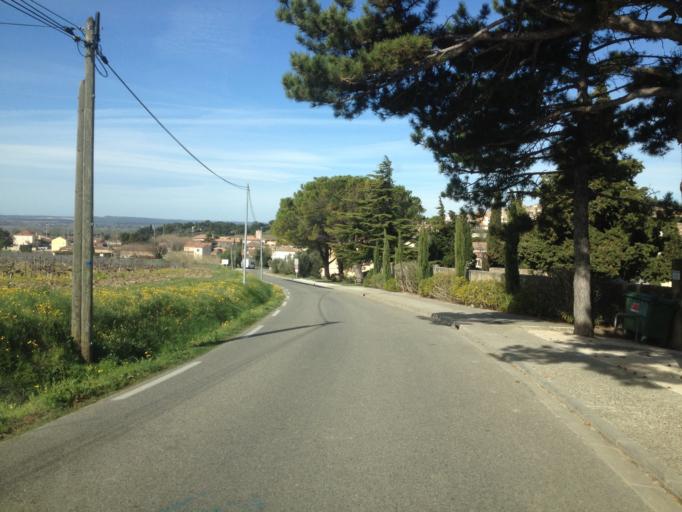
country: FR
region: Provence-Alpes-Cote d'Azur
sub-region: Departement du Vaucluse
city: Chateauneuf-du-Pape
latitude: 44.0546
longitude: 4.8396
